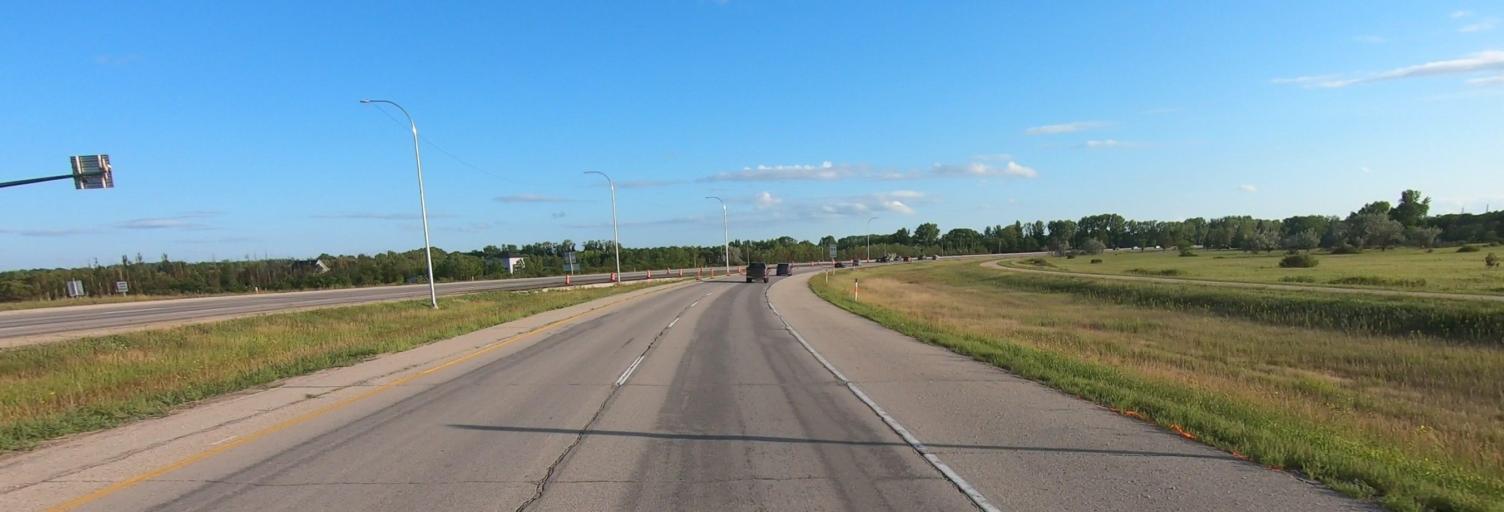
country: CA
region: Manitoba
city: Selkirk
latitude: 49.9730
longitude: -96.9722
